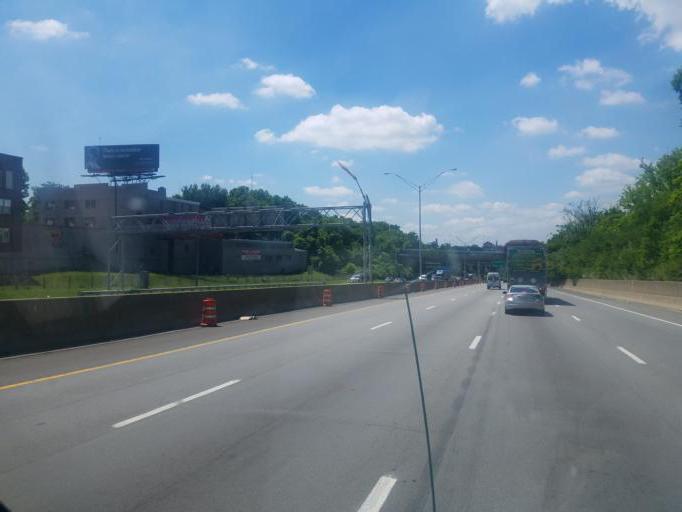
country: US
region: Kentucky
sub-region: Campbell County
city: Bellevue
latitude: 39.1248
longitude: -84.4978
